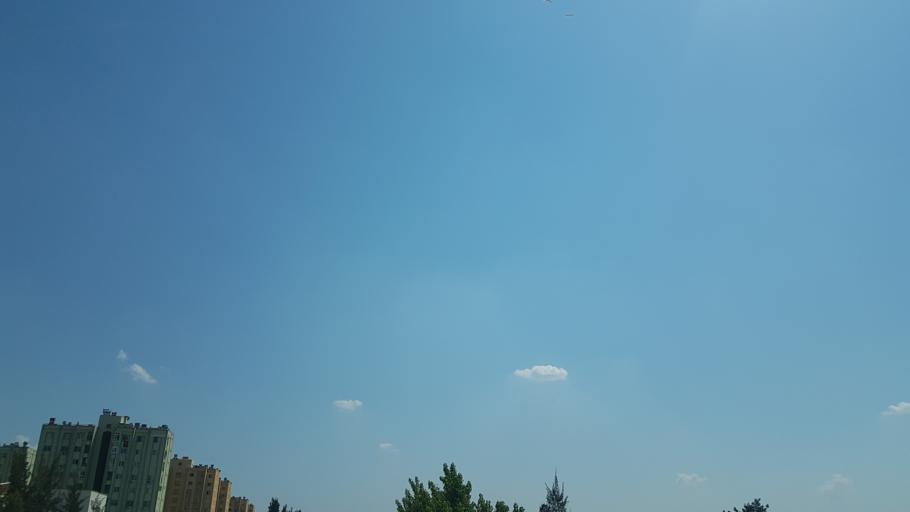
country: TR
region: Adana
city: Adana
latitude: 37.0297
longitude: 35.3551
